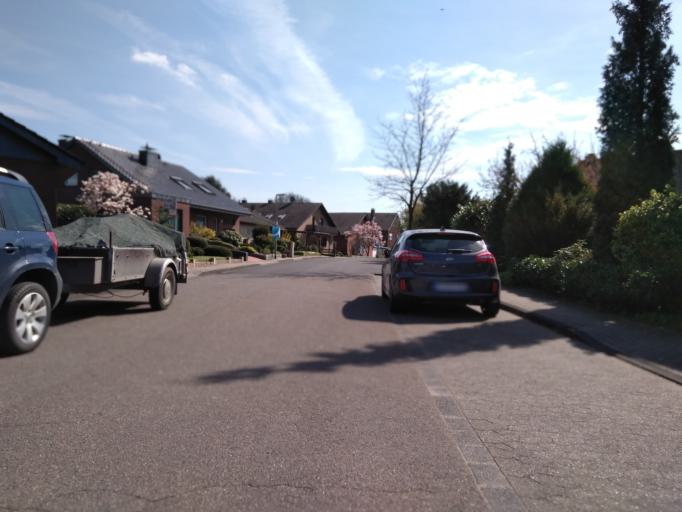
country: DE
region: North Rhine-Westphalia
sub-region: Regierungsbezirk Dusseldorf
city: Schermbeck
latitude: 51.6666
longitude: 6.8787
